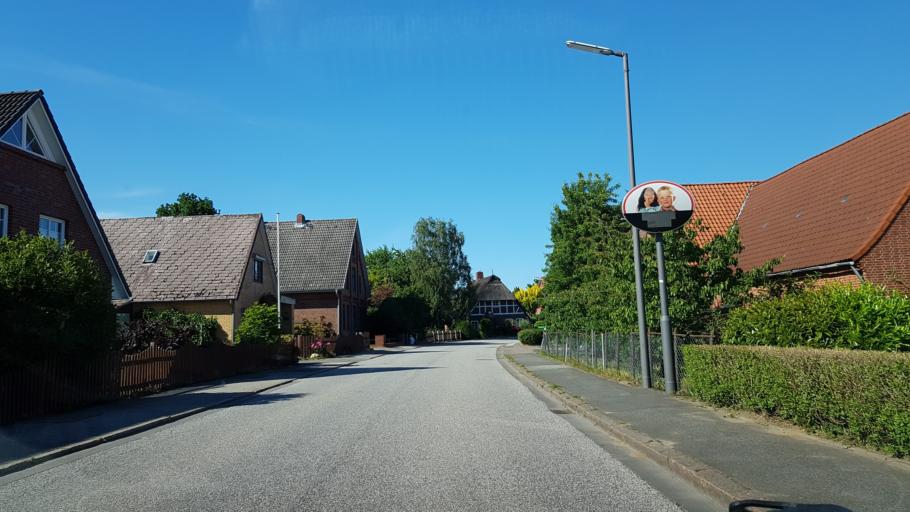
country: DE
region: Lower Saxony
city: Neu Wulmstorf
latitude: 53.5206
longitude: 9.7996
